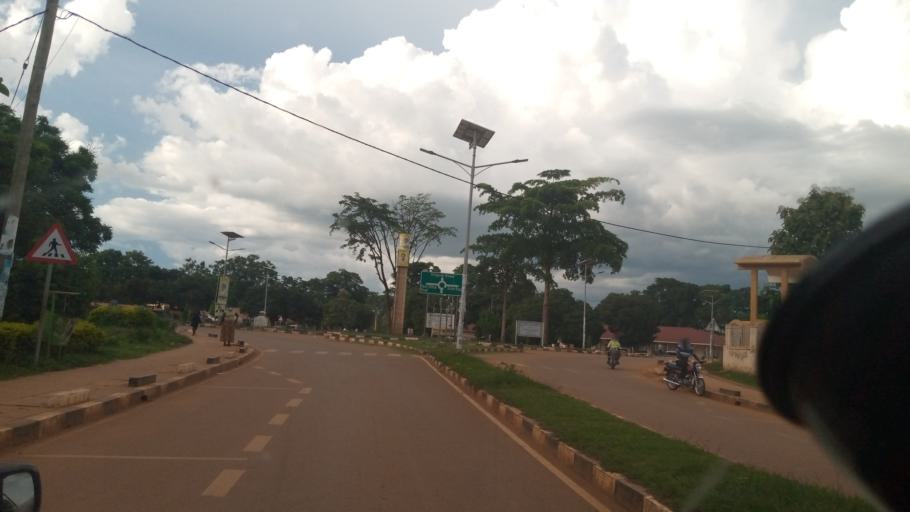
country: UG
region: Northern Region
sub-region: Lira District
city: Lira
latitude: 2.2478
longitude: 32.9001
